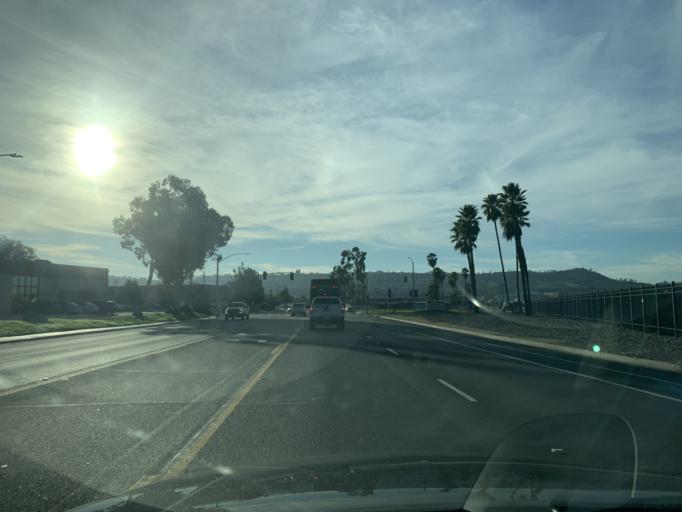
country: US
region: California
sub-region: San Diego County
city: Santee
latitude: 32.8181
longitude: -116.9667
